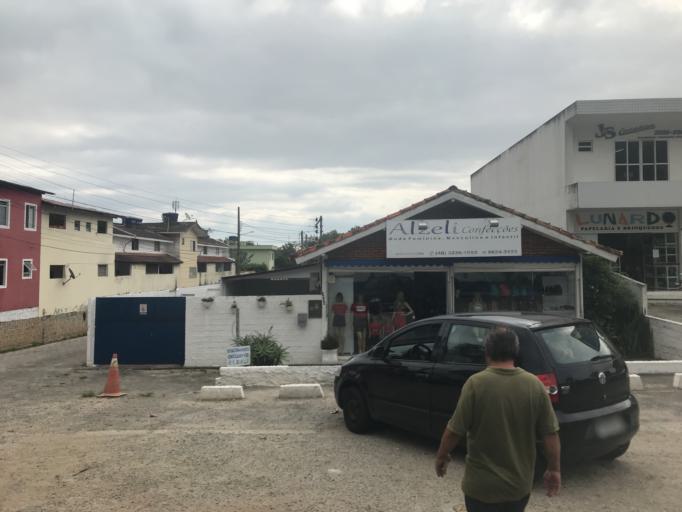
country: BR
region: Santa Catarina
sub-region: Florianopolis
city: Costeira do Pirajubae
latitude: -27.6331
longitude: -48.5236
